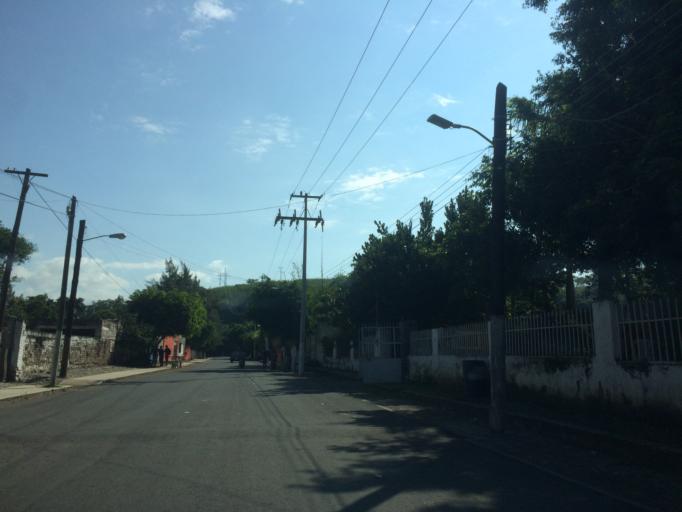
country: MX
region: Nayarit
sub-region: Ahuacatlan
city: Ahuacatlan
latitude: 21.0494
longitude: -104.4780
